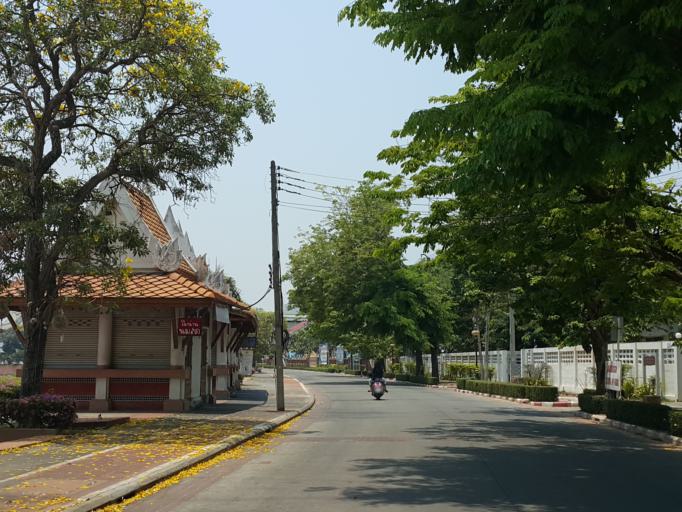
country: TH
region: Phitsanulok
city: Phitsanulok
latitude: 16.8219
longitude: 100.2585
